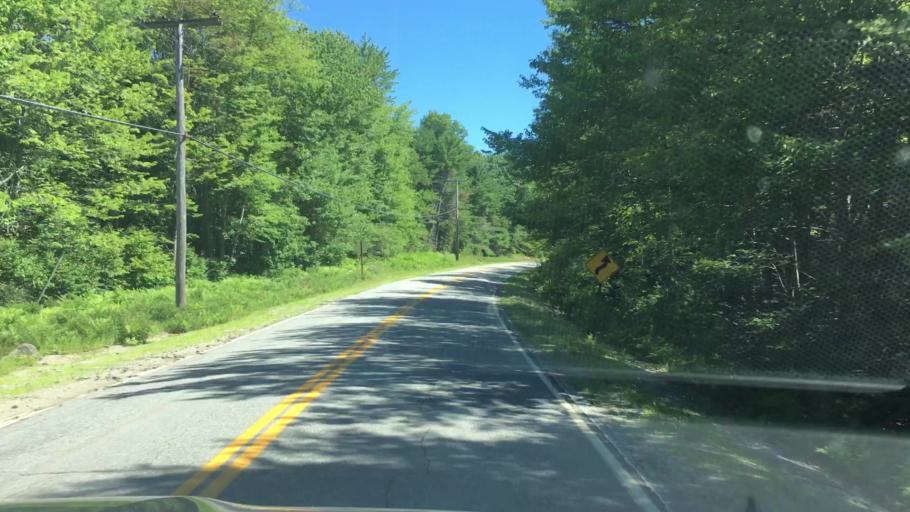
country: US
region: Maine
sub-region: Hancock County
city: Penobscot
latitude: 44.4754
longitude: -68.6959
